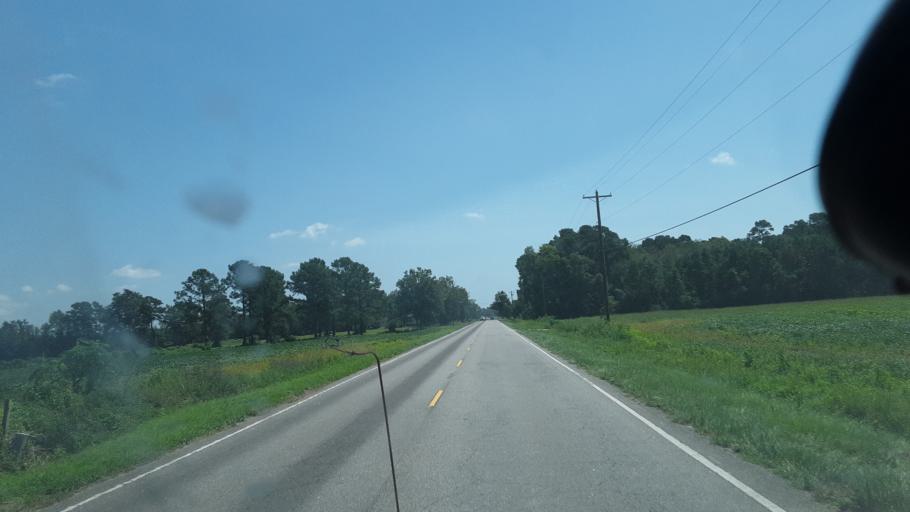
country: US
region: South Carolina
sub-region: Horry County
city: North Myrtle Beach
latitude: 33.8580
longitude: -78.7196
